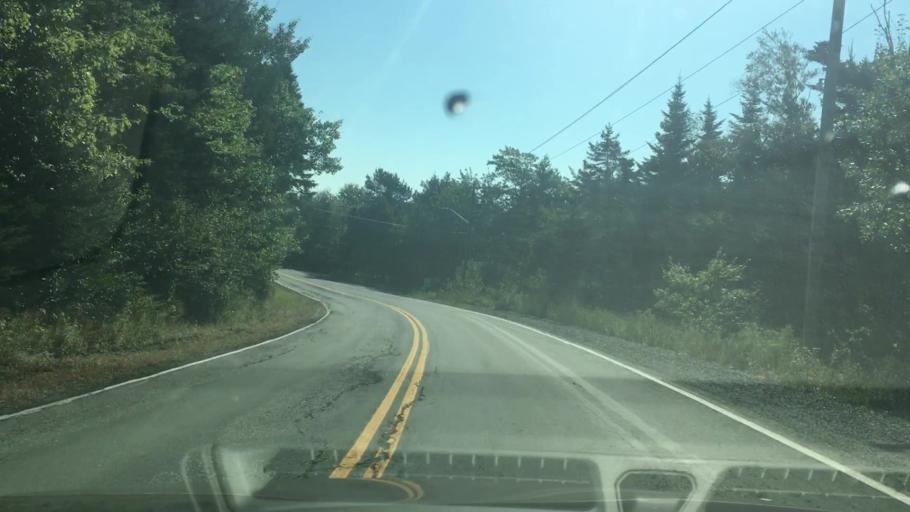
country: CA
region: Nova Scotia
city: Cole Harbour
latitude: 44.7768
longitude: -63.0720
